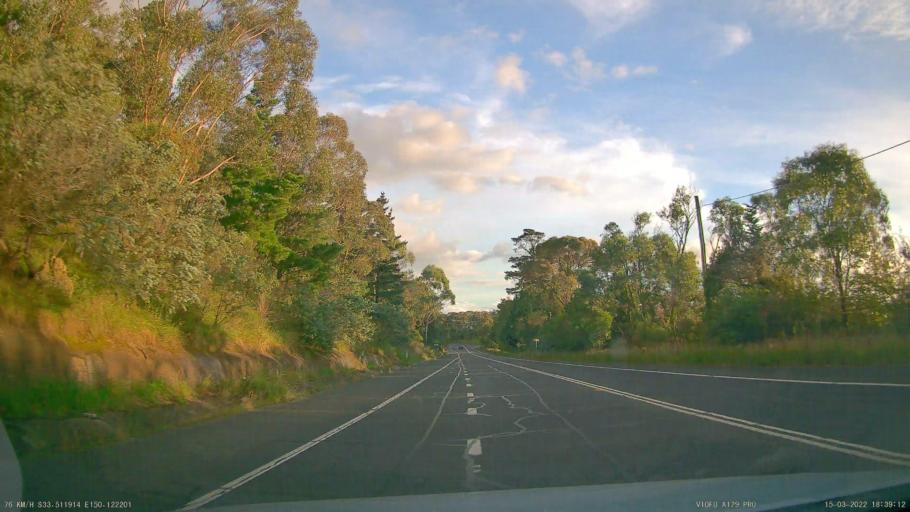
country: AU
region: New South Wales
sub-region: Lithgow
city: Bowenfels
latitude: -33.5123
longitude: 150.1221
